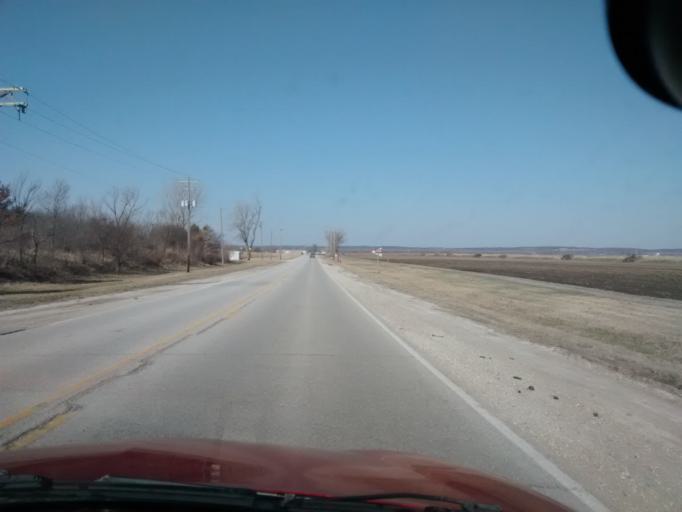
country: US
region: Iowa
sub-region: Pottawattamie County
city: Carter Lake
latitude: 41.3623
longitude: -95.8626
